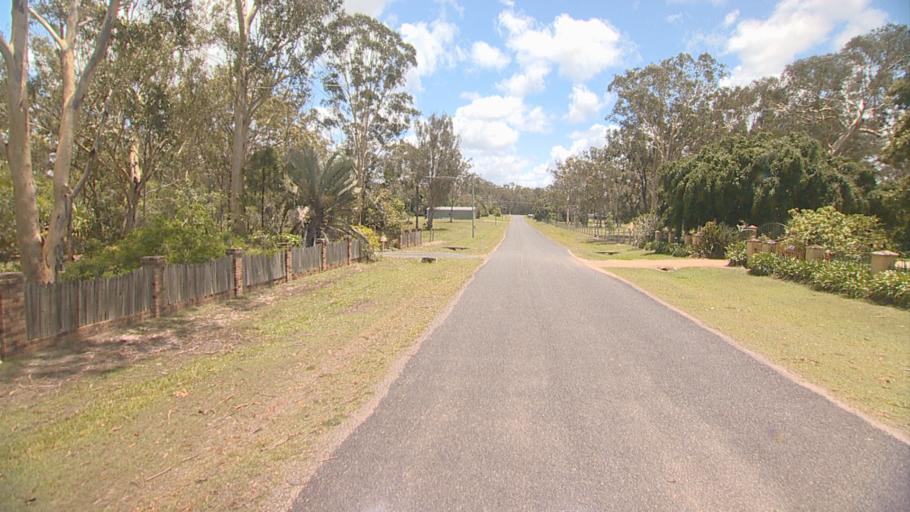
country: AU
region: Queensland
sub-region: Redland
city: Redland Bay
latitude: -27.6793
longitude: 153.2784
